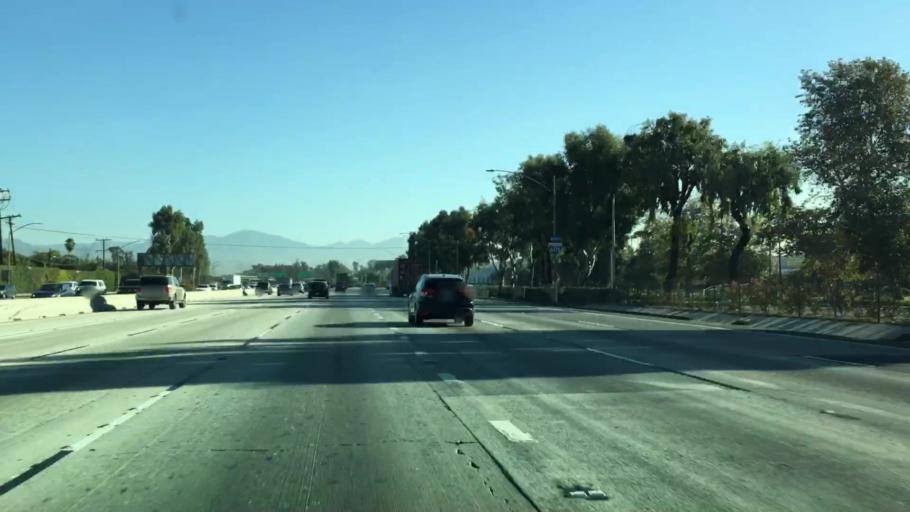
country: US
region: California
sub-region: Los Angeles County
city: South El Monte
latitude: 34.0290
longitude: -118.0343
